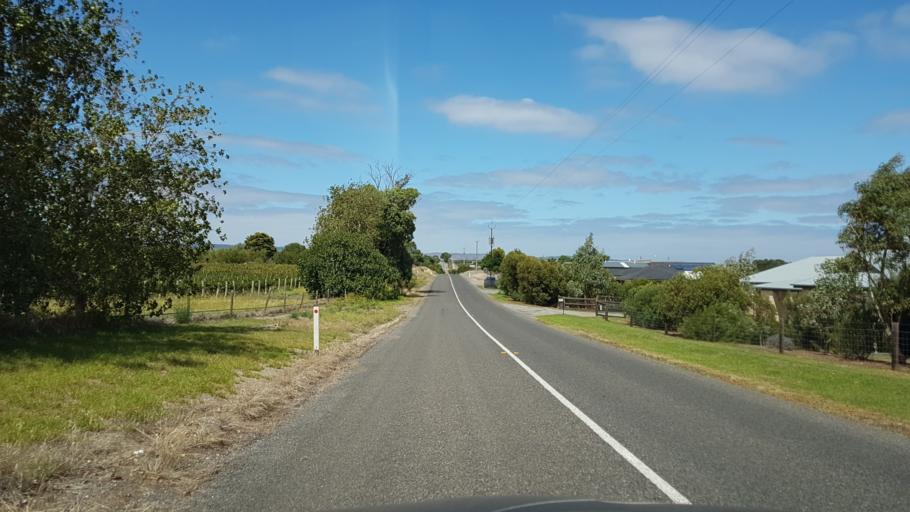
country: AU
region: South Australia
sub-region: Onkaparinga
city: McLaren Vale
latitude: -35.2160
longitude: 138.5177
